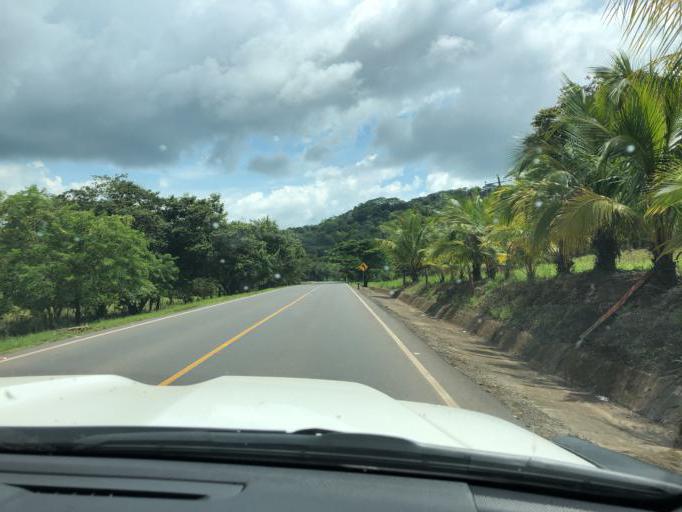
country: NI
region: Chontales
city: Villa Sandino
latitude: 12.0570
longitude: -85.0398
